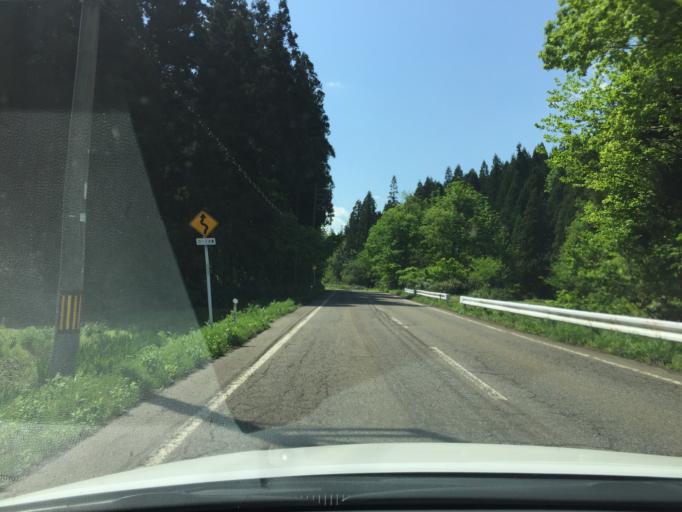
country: JP
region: Niigata
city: Tochio-honcho
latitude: 37.5377
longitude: 139.0920
